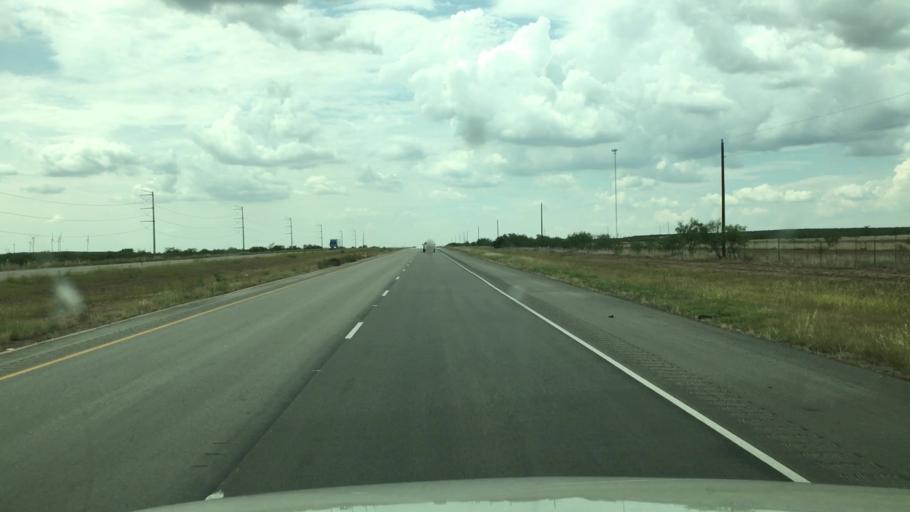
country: US
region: Texas
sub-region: Glasscock County
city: Garden City
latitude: 31.9753
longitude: -101.2478
